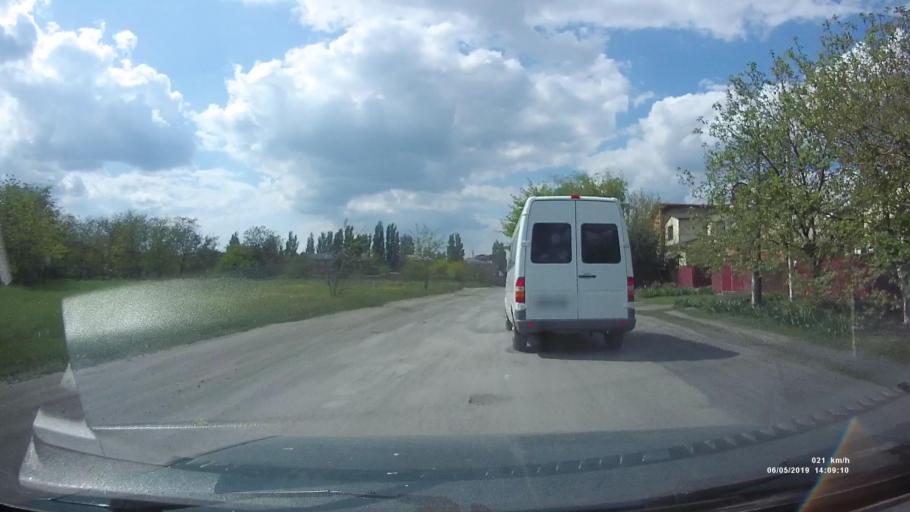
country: RU
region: Rostov
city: Shakhty
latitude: 47.6855
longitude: 40.2926
